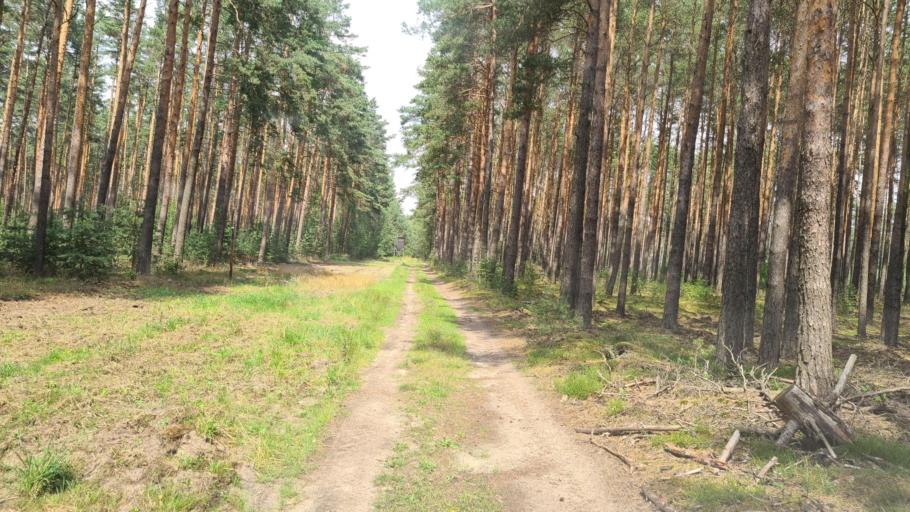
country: DE
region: Brandenburg
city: Bronkow
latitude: 51.7175
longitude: 13.8781
